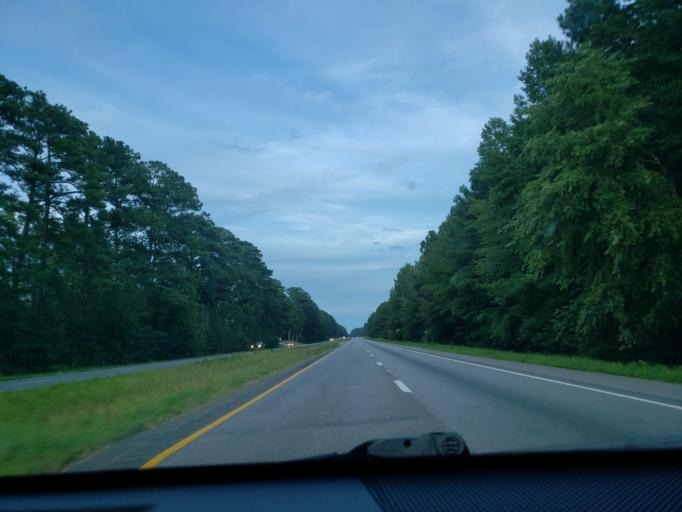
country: US
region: Virginia
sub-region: Sussex County
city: Sussex
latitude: 36.7060
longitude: -77.2925
